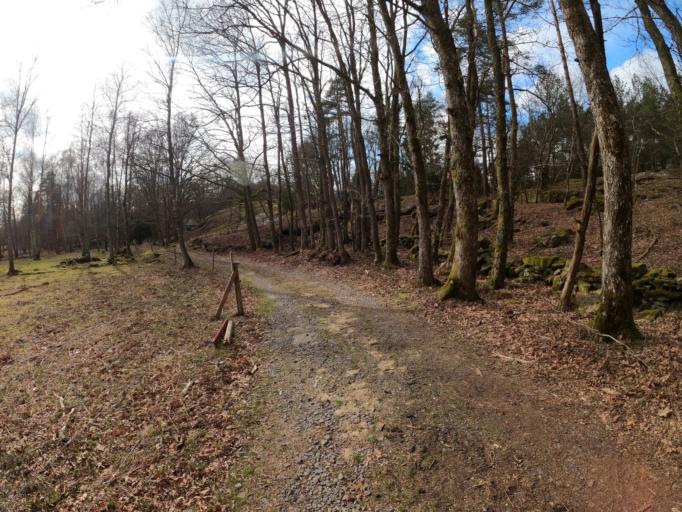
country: SE
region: Vaestra Goetaland
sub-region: Harryda Kommun
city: Molnlycke
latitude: 57.6315
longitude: 12.0882
